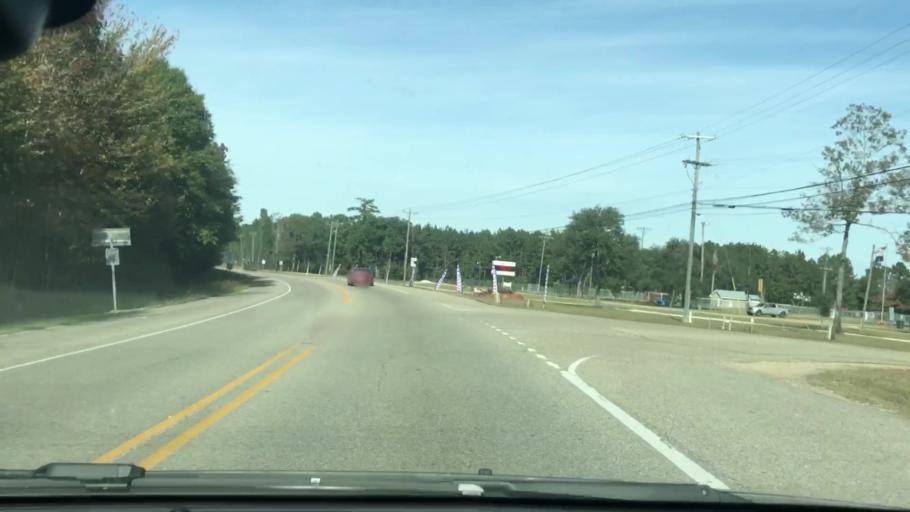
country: US
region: Louisiana
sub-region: Saint Tammany Parish
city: Pearl River
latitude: 30.3918
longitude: -89.7617
